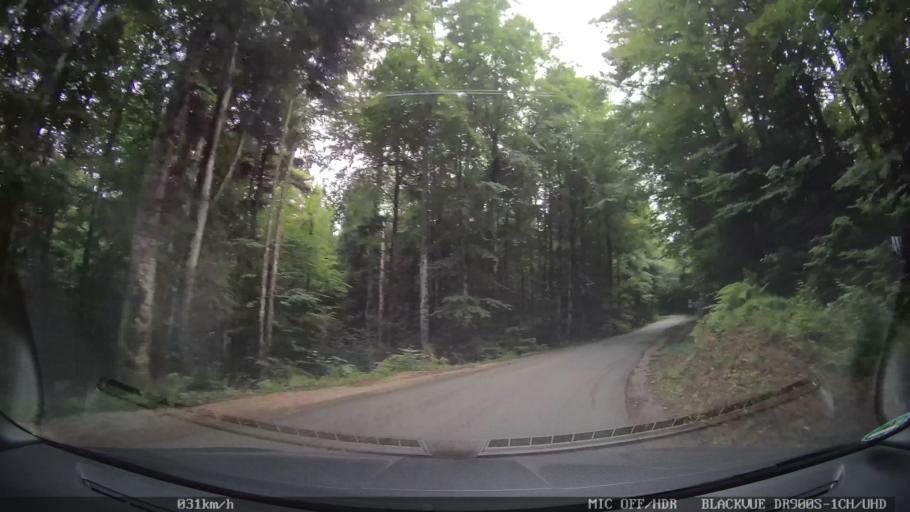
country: HR
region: Licko-Senjska
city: Jezerce
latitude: 44.9275
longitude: 15.5748
